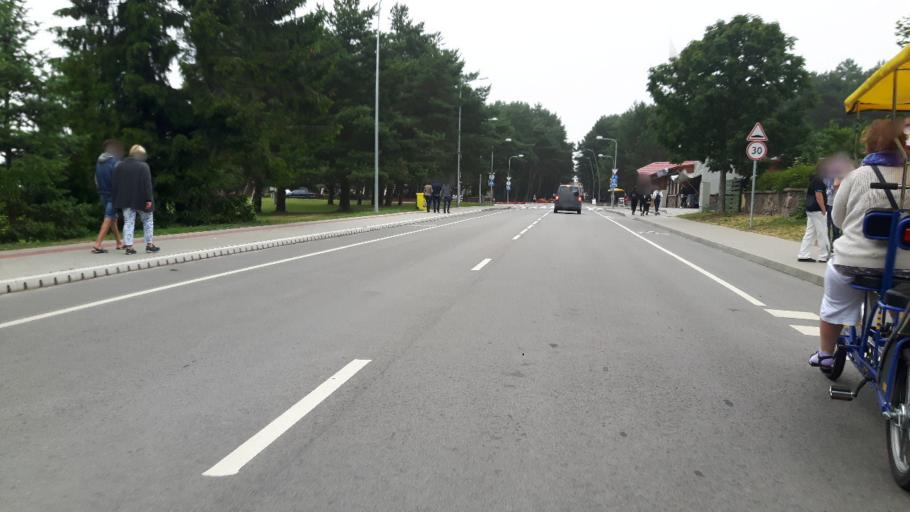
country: LT
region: Klaipedos apskritis
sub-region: Palanga
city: Sventoji
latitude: 56.0263
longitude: 21.0797
